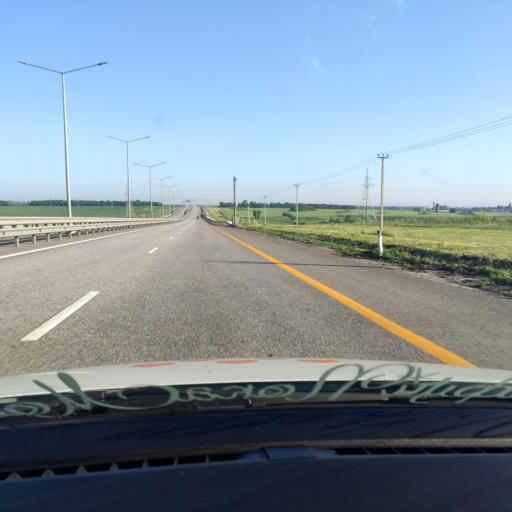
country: RU
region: Voronezj
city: Kashirskoye
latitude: 51.4899
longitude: 39.5315
